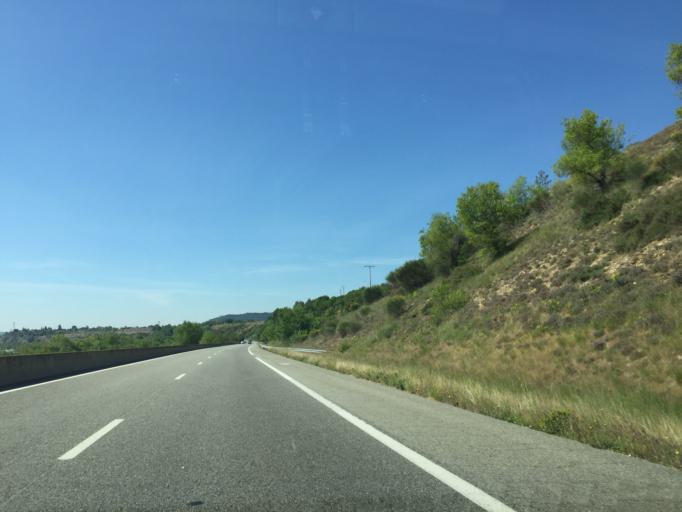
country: FR
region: Provence-Alpes-Cote d'Azur
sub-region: Departement des Alpes-de-Haute-Provence
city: Oraison
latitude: 43.9483
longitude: 5.8959
